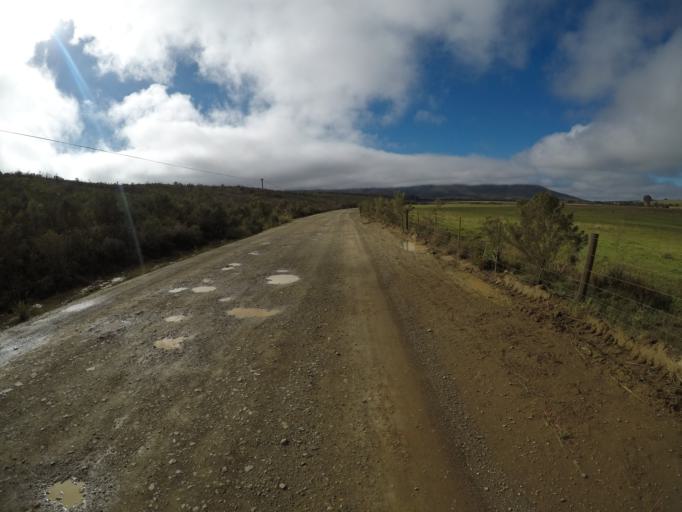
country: ZA
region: Western Cape
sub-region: Cape Winelands District Municipality
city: Ashton
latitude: -34.1246
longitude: 19.8263
